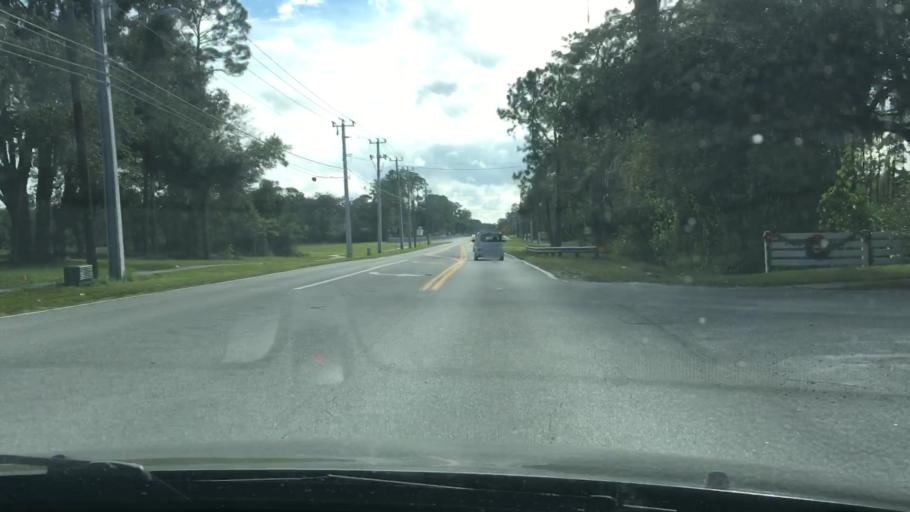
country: US
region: Florida
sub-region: Volusia County
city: Ormond Beach
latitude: 29.2669
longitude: -81.1293
